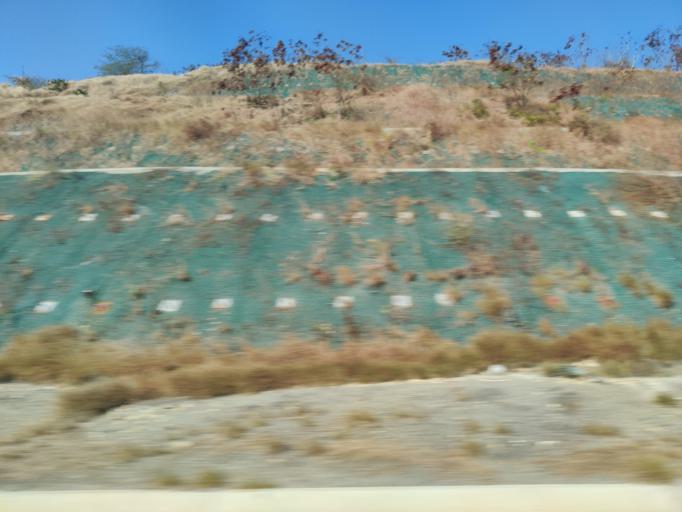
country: CO
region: Atlantico
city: Puerto Colombia
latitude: 10.9498
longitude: -75.0035
